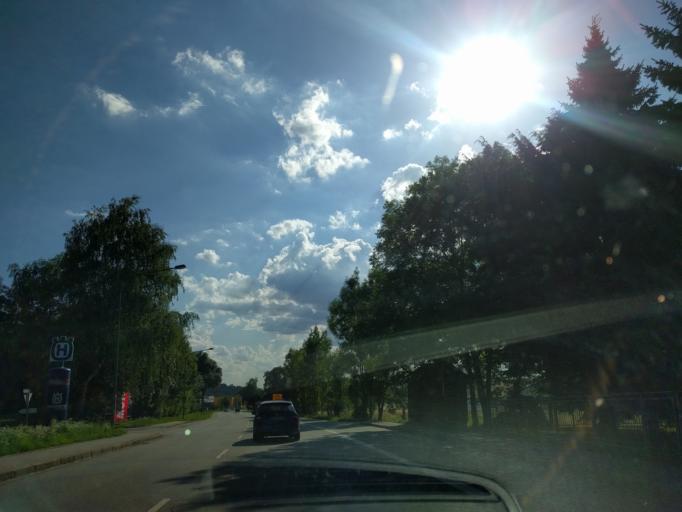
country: DE
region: Bavaria
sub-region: Lower Bavaria
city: Deggendorf
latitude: 48.8524
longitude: 12.9906
